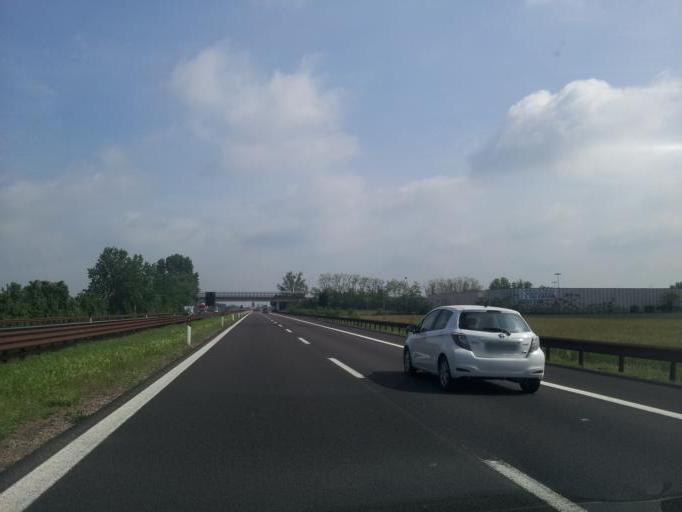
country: IT
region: Lombardy
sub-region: Provincia di Mantova
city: Bondeno
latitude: 44.9300
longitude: 10.8587
